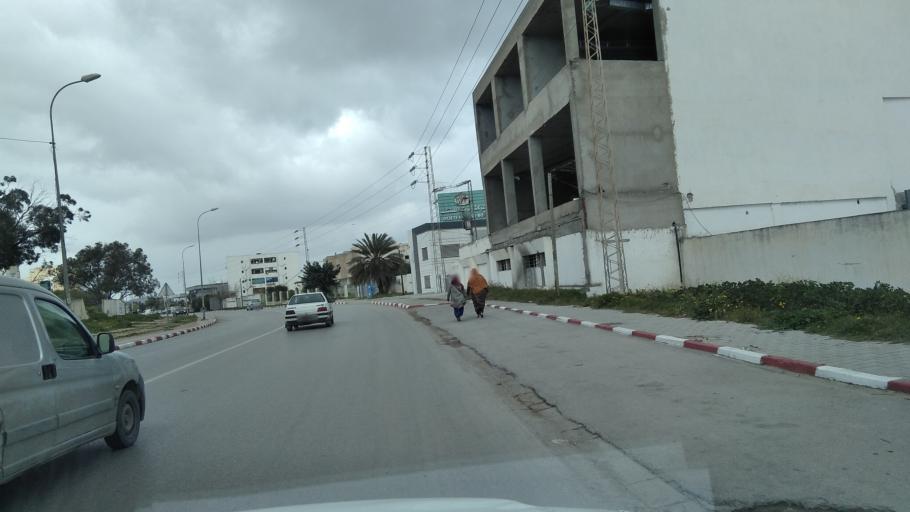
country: TN
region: Bin 'Arus
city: Ben Arous
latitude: 36.7454
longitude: 10.2334
